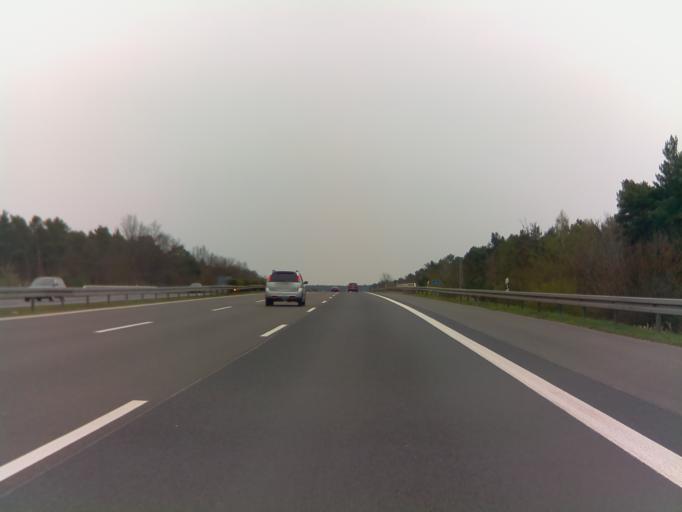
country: DE
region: Brandenburg
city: Fichtenwalde
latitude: 52.2559
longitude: 12.9090
